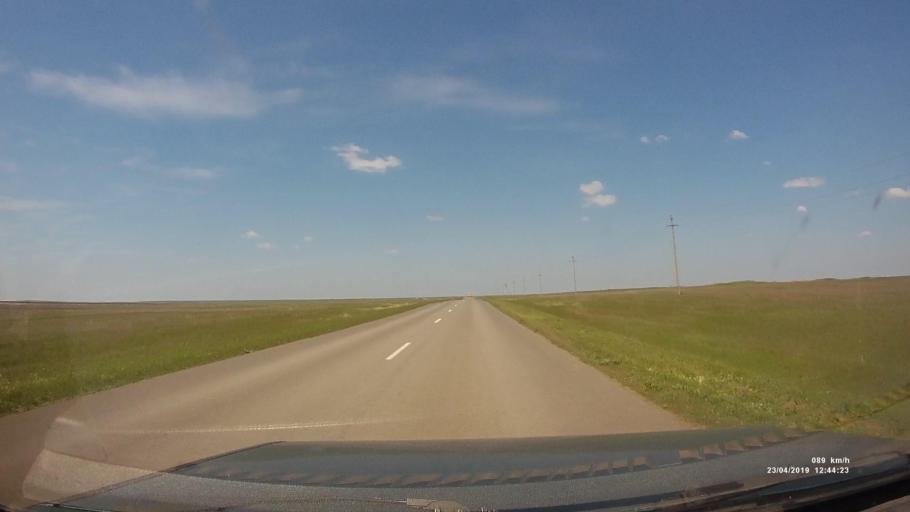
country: RU
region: Kalmykiya
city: Yashalta
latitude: 46.4761
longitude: 42.6477
